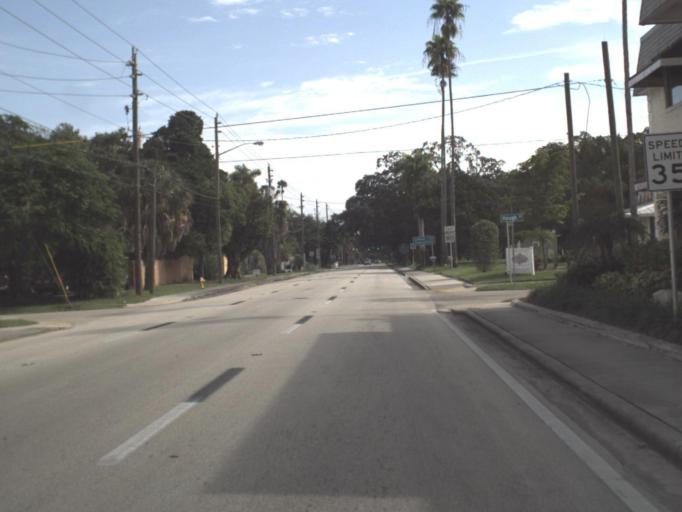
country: US
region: Florida
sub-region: Lee County
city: North Fort Myers
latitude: 26.6448
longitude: -81.8645
